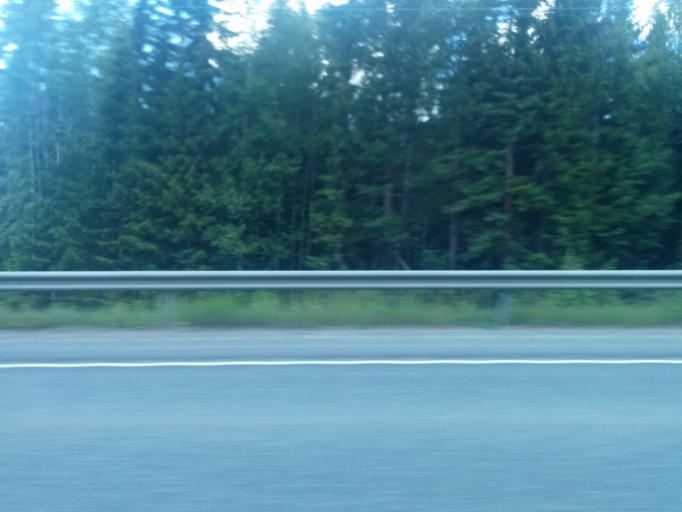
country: FI
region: Pirkanmaa
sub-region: Tampere
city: Kangasala
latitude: 61.5363
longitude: 23.9621
